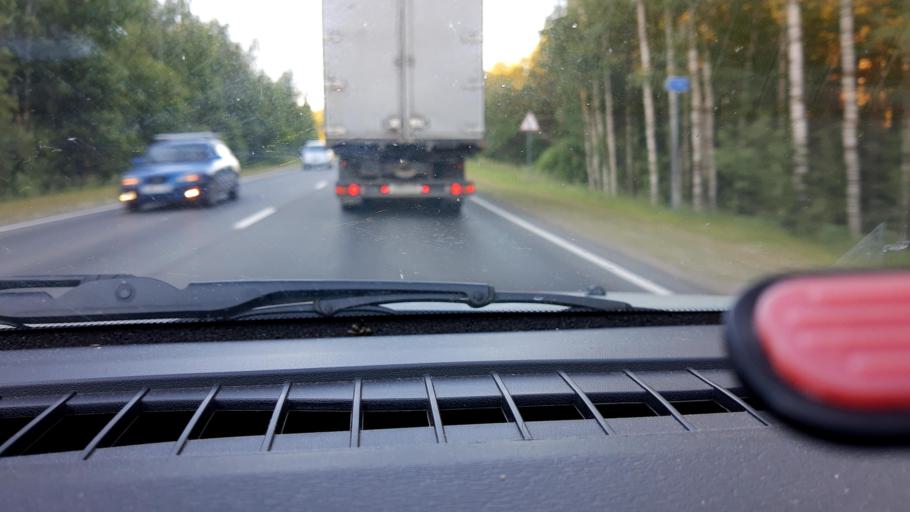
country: RU
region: Nizjnij Novgorod
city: Semenov
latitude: 56.7819
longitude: 44.4358
